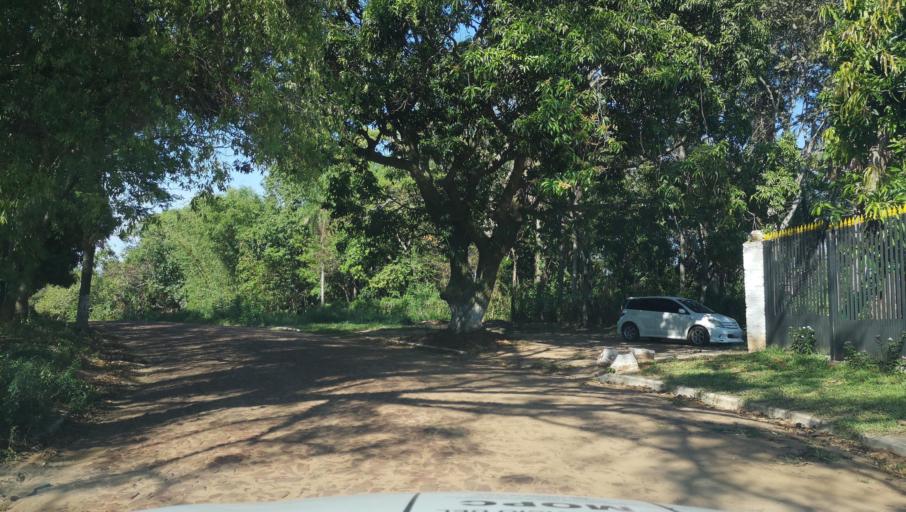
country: PY
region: Misiones
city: Santa Maria
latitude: -26.8774
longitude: -57.0091
